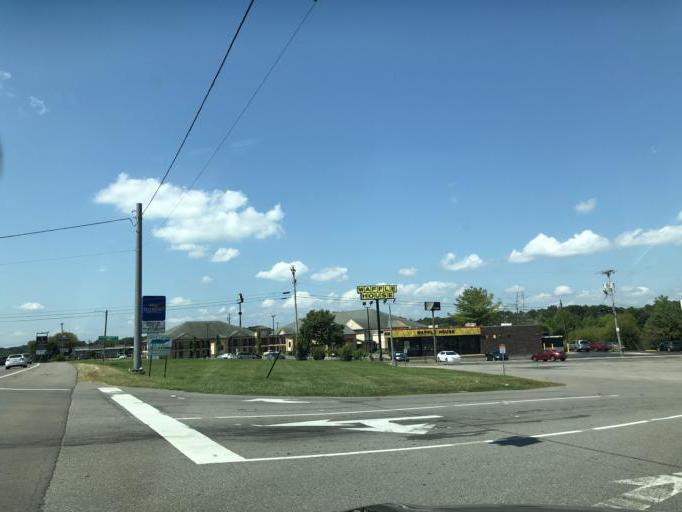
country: US
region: Tennessee
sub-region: Montgomery County
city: Clarksville
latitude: 36.5249
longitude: -87.2250
